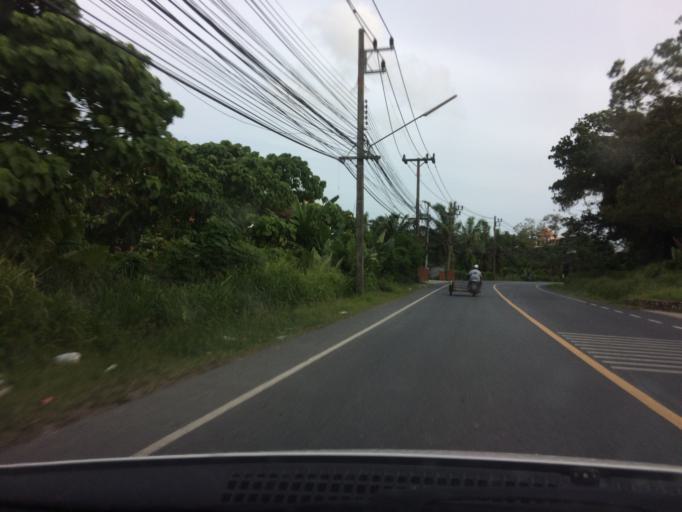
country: TH
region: Phuket
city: Ban Ratsada
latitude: 7.8985
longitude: 98.4107
